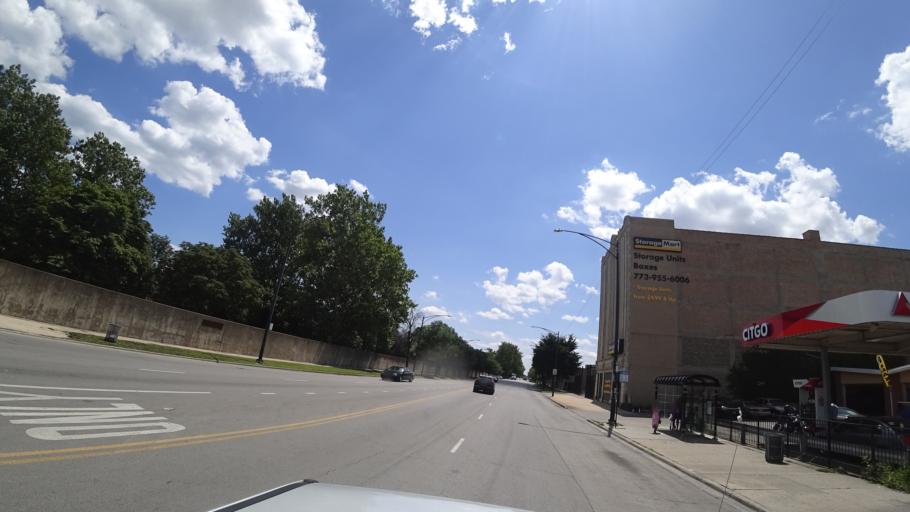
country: US
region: Illinois
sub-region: Cook County
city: Chicago
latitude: 41.7730
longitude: -87.6058
